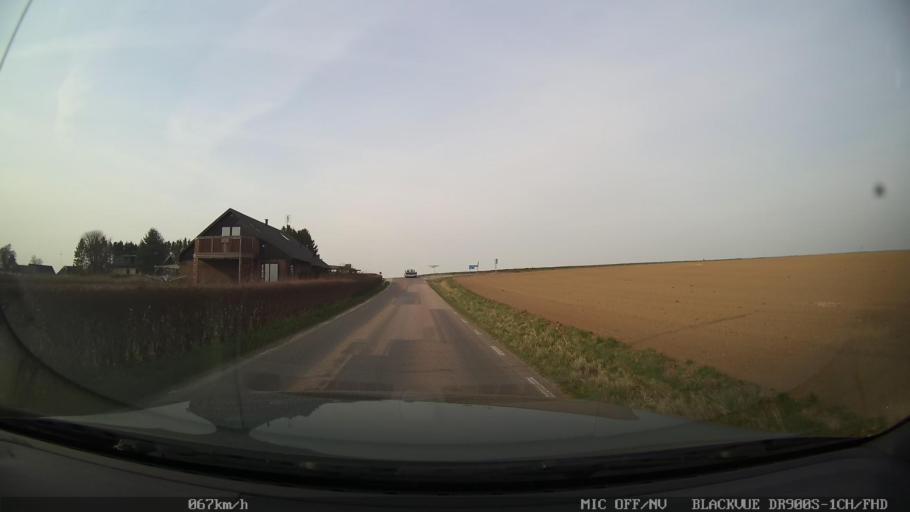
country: SE
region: Skane
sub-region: Ystads Kommun
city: Ystad
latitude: 55.4538
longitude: 13.8304
